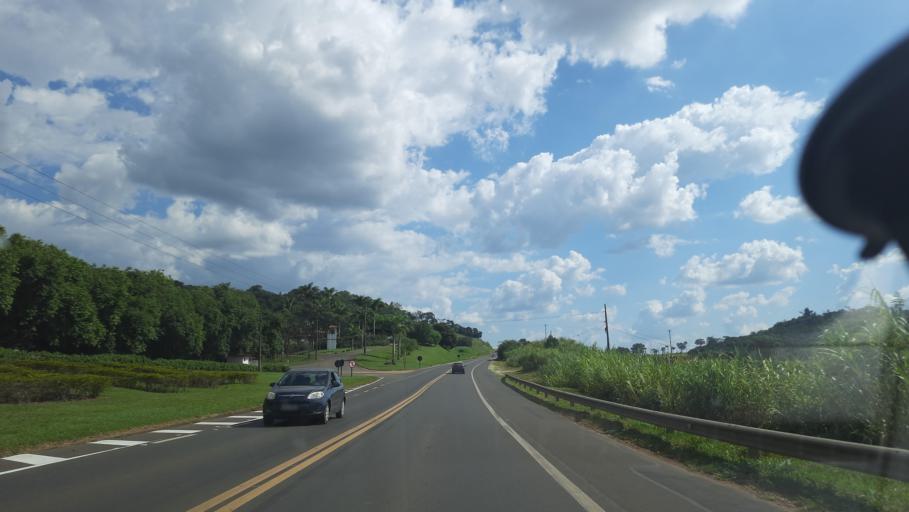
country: BR
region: Sao Paulo
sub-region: Sao Jose Do Rio Pardo
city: Sao Jose do Rio Pardo
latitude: -21.6495
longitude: -46.9102
